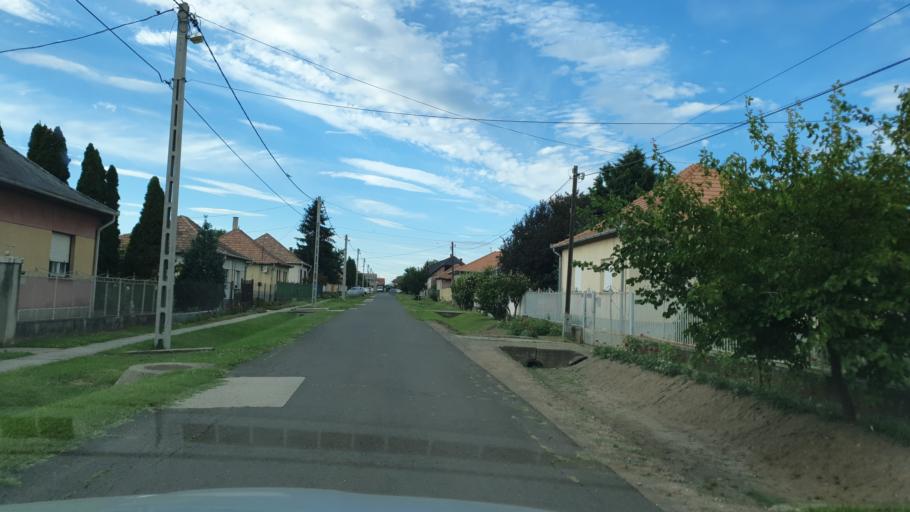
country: HU
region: Heves
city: Zagyvaszanto
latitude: 47.7694
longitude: 19.6647
